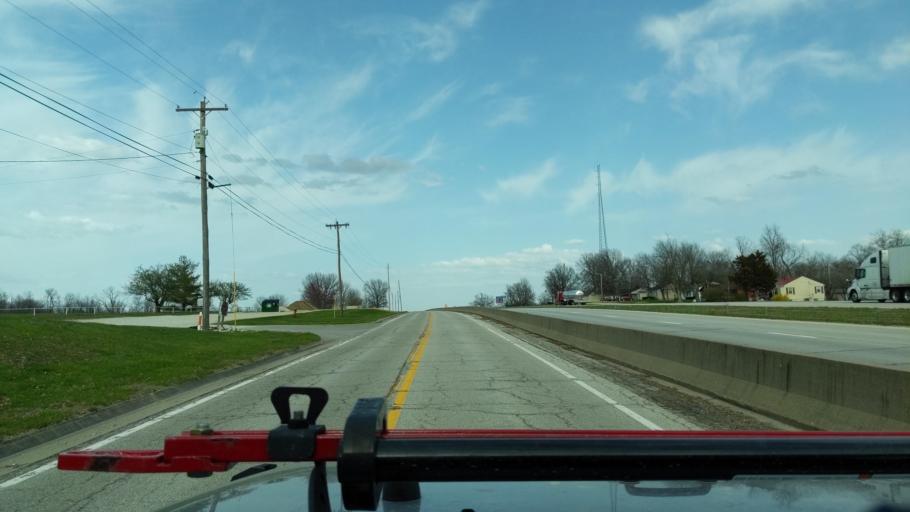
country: US
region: Missouri
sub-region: Macon County
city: Macon
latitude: 39.7495
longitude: -92.4819
